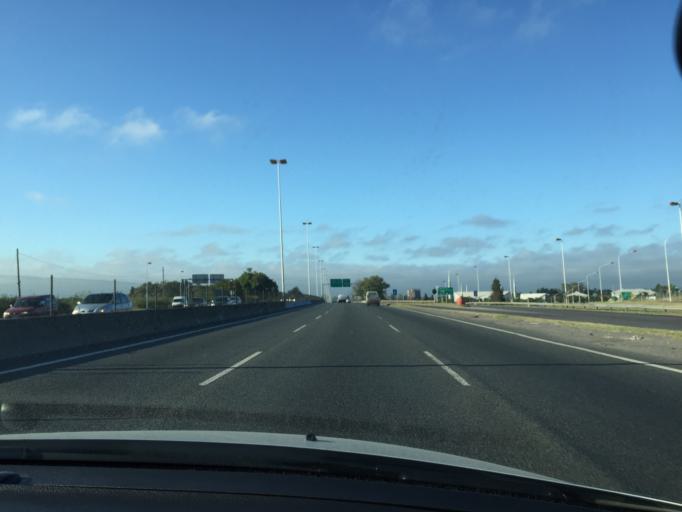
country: AR
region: Buenos Aires F.D.
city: Villa Lugano
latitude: -34.7246
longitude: -58.5146
